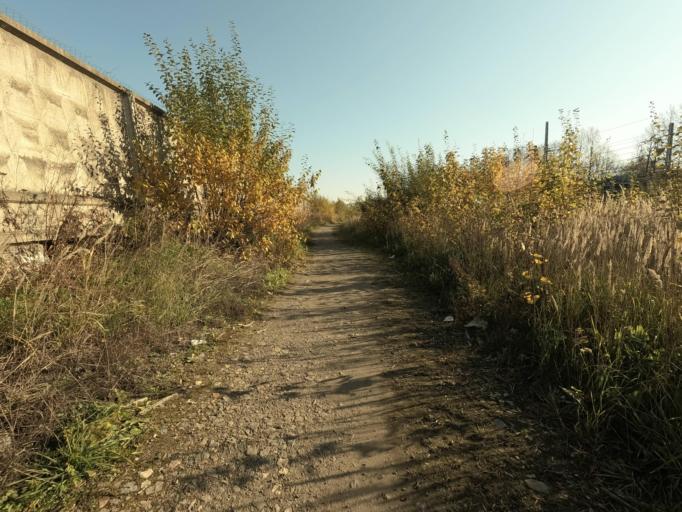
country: RU
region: St.-Petersburg
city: Obukhovo
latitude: 59.8435
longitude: 30.4697
